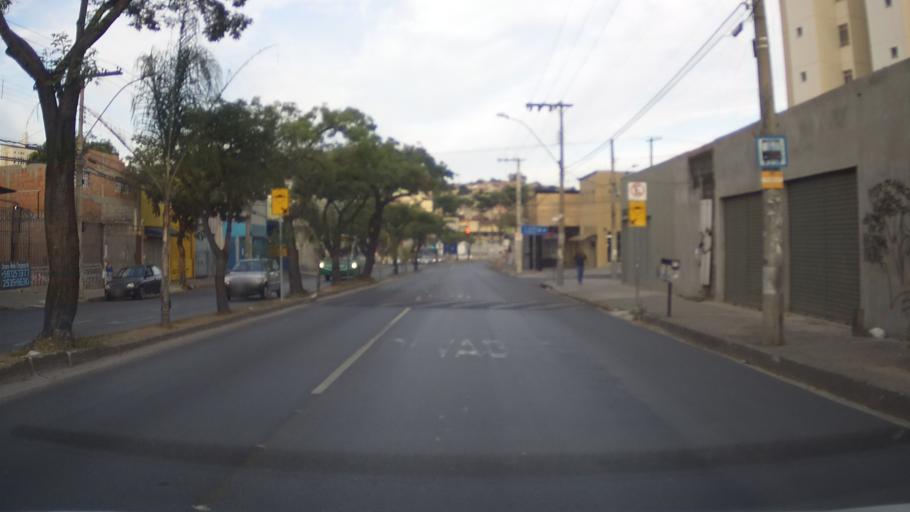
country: BR
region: Minas Gerais
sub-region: Contagem
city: Contagem
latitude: -19.9130
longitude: -43.9997
